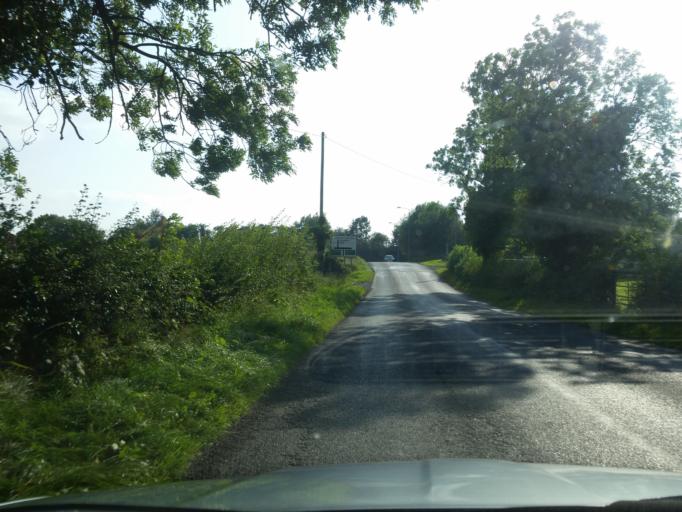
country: GB
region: Northern Ireland
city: Lisnaskea
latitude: 54.2991
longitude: -7.4666
